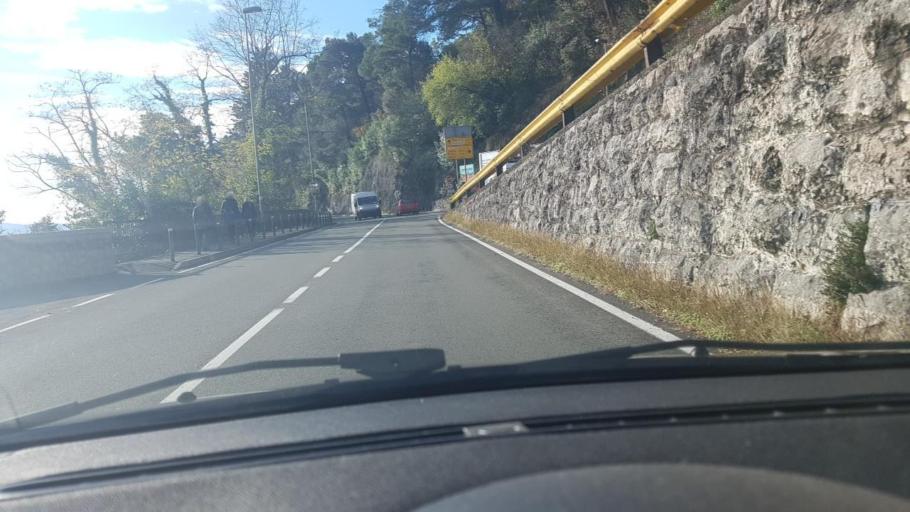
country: HR
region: Primorsko-Goranska
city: Matulji
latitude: 45.3546
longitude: 14.3252
